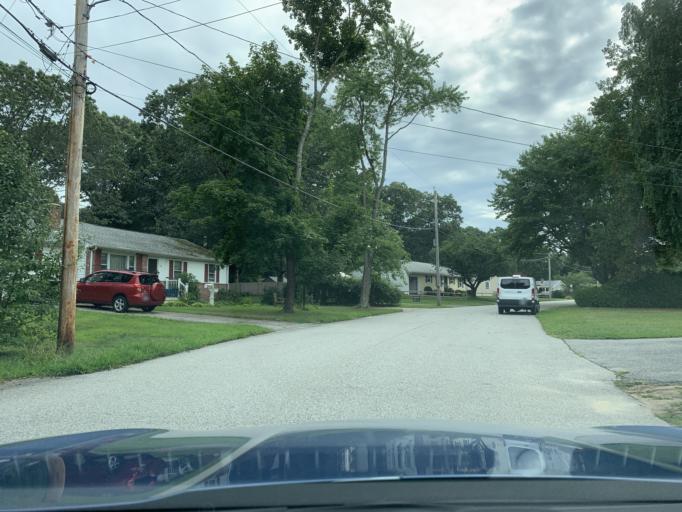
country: US
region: Rhode Island
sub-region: Kent County
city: East Greenwich
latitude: 41.6170
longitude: -71.4649
